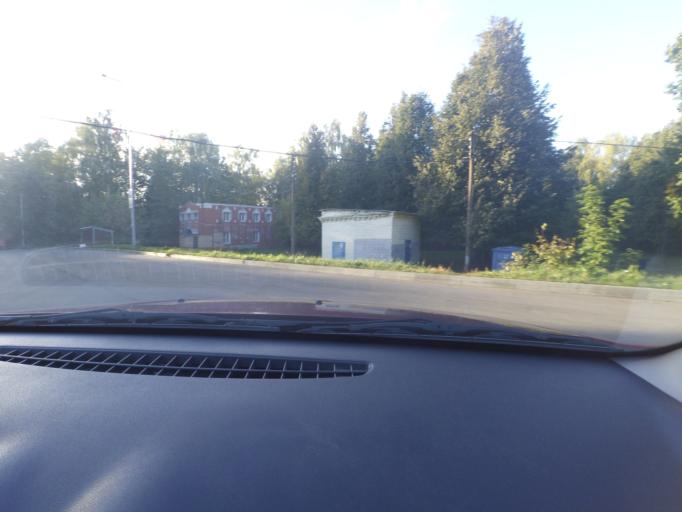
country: RU
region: Nizjnij Novgorod
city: Nizhniy Novgorod
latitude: 56.2927
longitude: 44.0065
